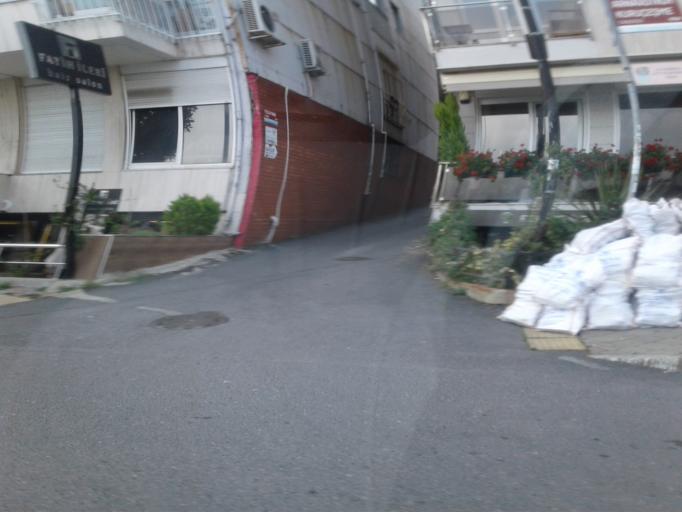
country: TR
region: Istanbul
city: UEskuedar
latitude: 41.0635
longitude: 29.0406
